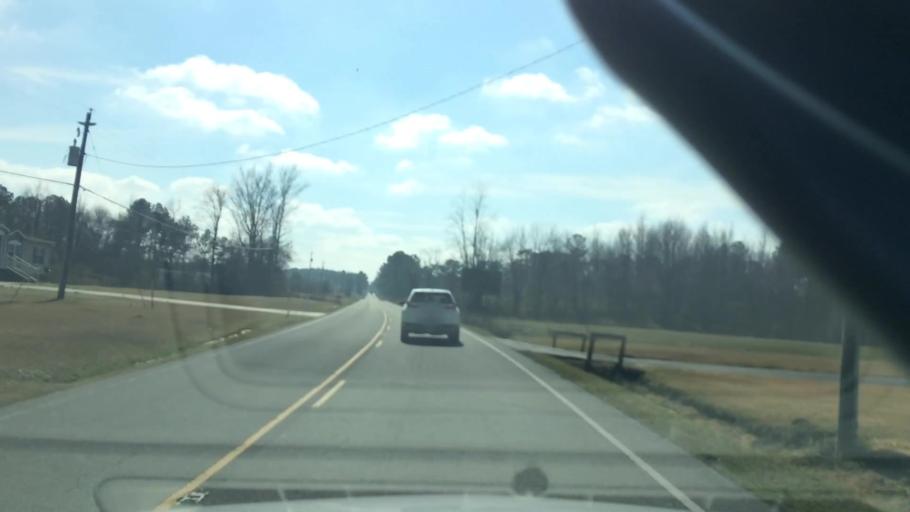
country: US
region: North Carolina
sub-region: Duplin County
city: Beulaville
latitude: 34.8812
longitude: -77.7892
